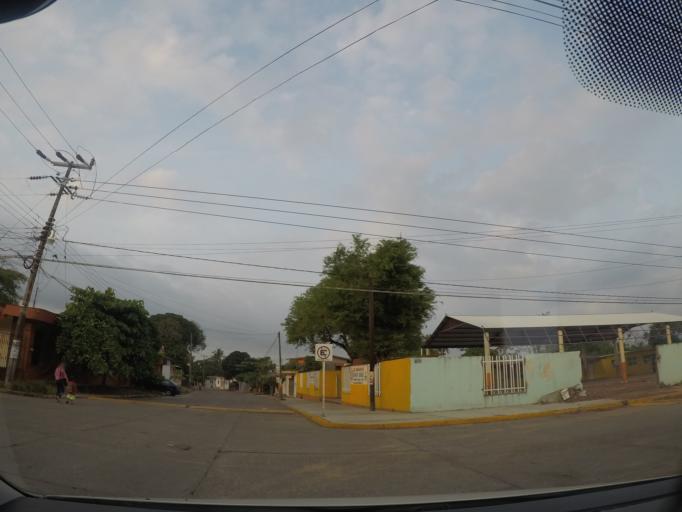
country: MX
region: Oaxaca
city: Matias Romero
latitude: 16.8731
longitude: -95.0351
